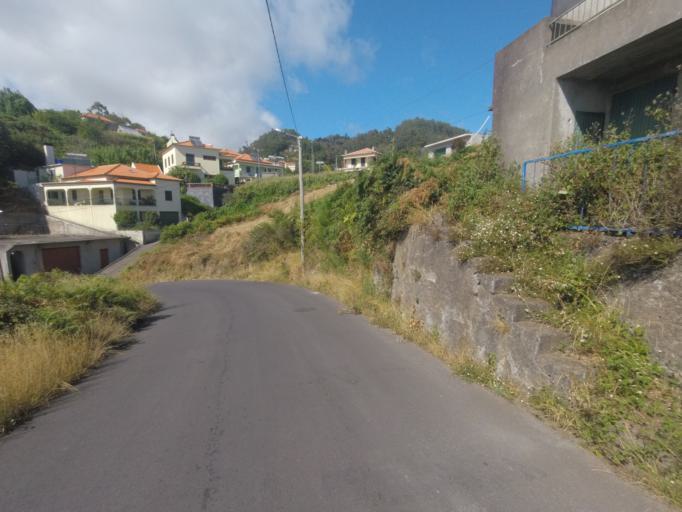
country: PT
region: Madeira
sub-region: Ribeira Brava
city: Campanario
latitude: 32.7013
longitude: -17.0212
